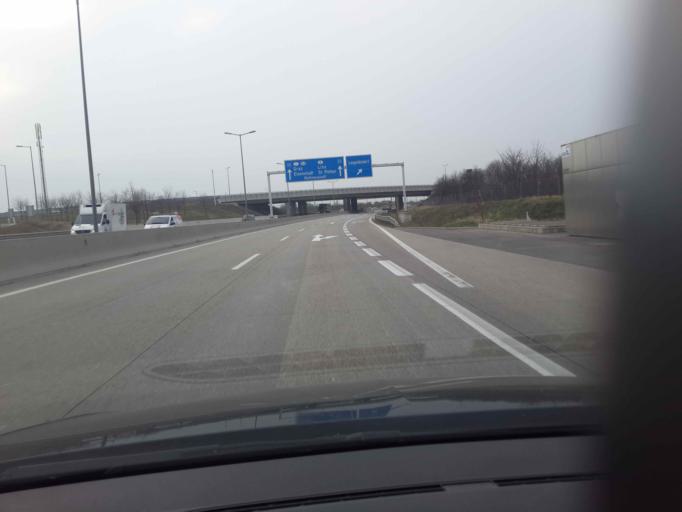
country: AT
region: Lower Austria
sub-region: Politischer Bezirk Wien-Umgebung
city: Leopoldsdorf
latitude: 48.1200
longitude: 16.4145
